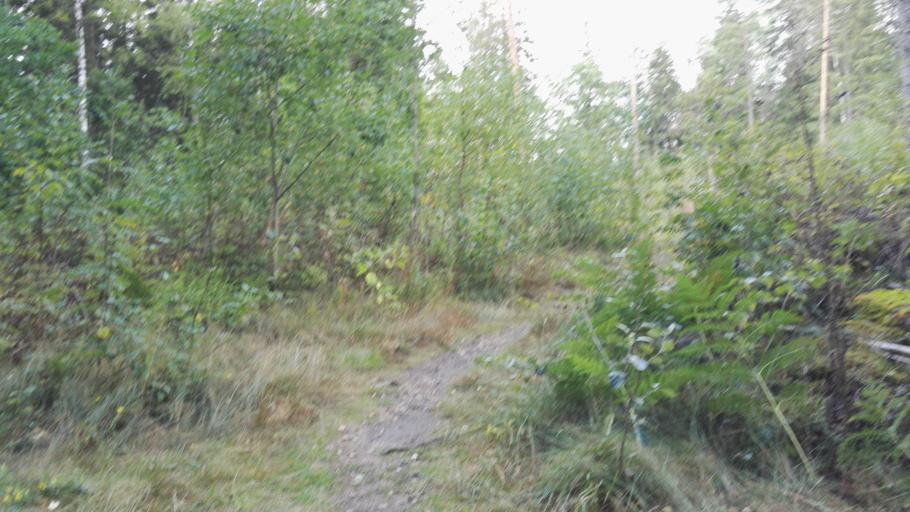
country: SE
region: Joenkoeping
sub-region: Vetlanda Kommun
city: Landsbro
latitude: 57.2346
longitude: 14.8546
